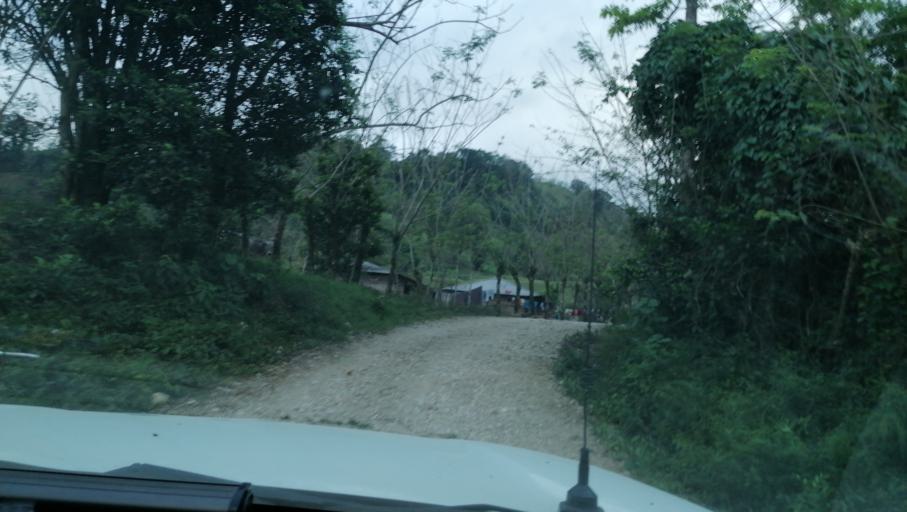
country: MX
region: Chiapas
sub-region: Francisco Leon
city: San Miguel la Sardina
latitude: 17.3055
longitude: -93.2673
